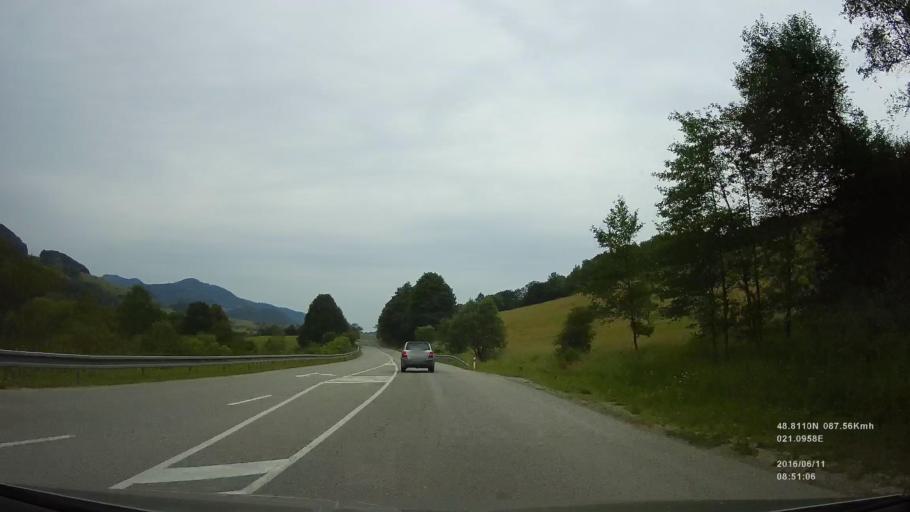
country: SK
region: Kosicky
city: Gelnica
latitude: 48.8043
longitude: 21.1007
